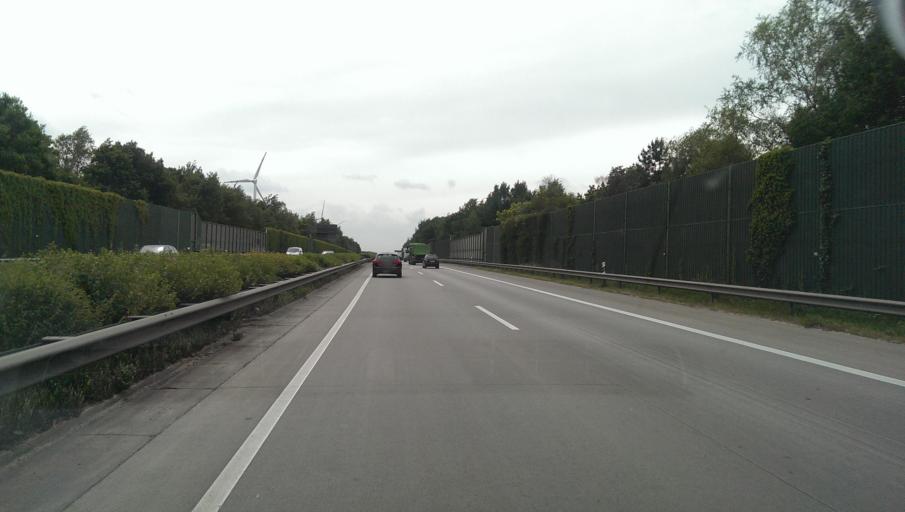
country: DE
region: Lower Saxony
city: Langen
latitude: 53.5718
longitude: 8.6197
